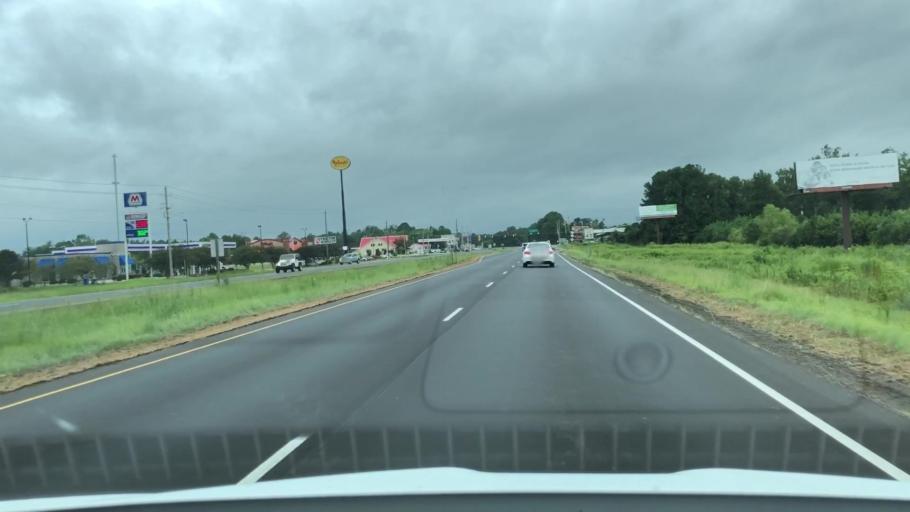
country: US
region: North Carolina
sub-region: Lenoir County
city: Kinston
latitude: 35.2520
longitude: -77.5985
